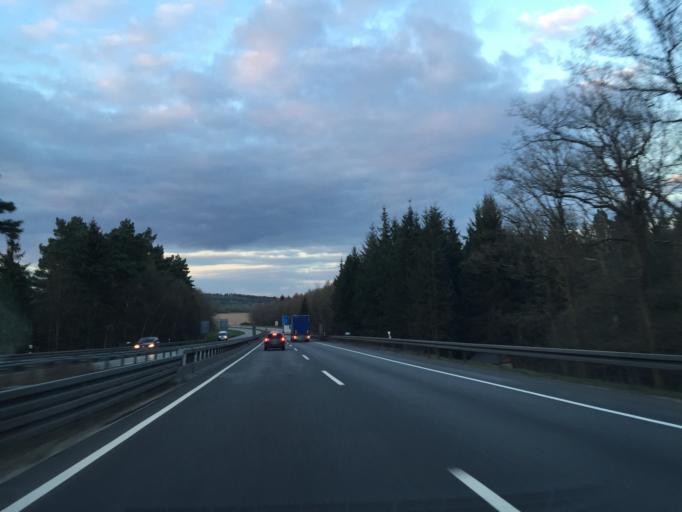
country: DE
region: Thuringia
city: Grossensee
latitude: 50.9312
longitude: 9.9198
